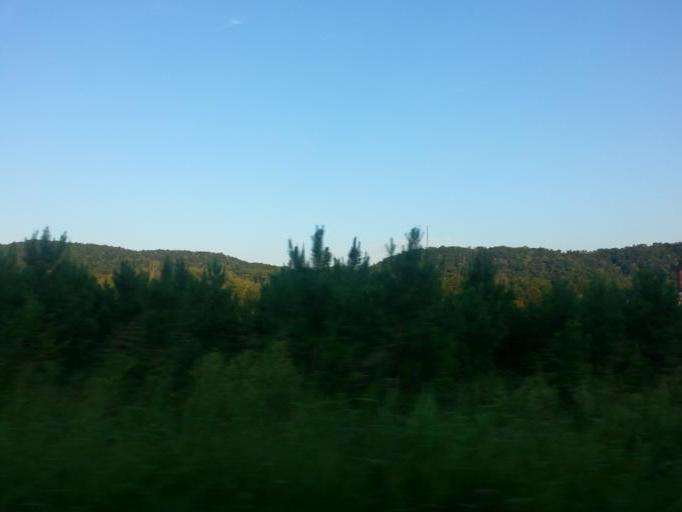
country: US
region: Tennessee
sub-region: Roane County
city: Midtown
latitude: 35.7956
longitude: -84.5698
